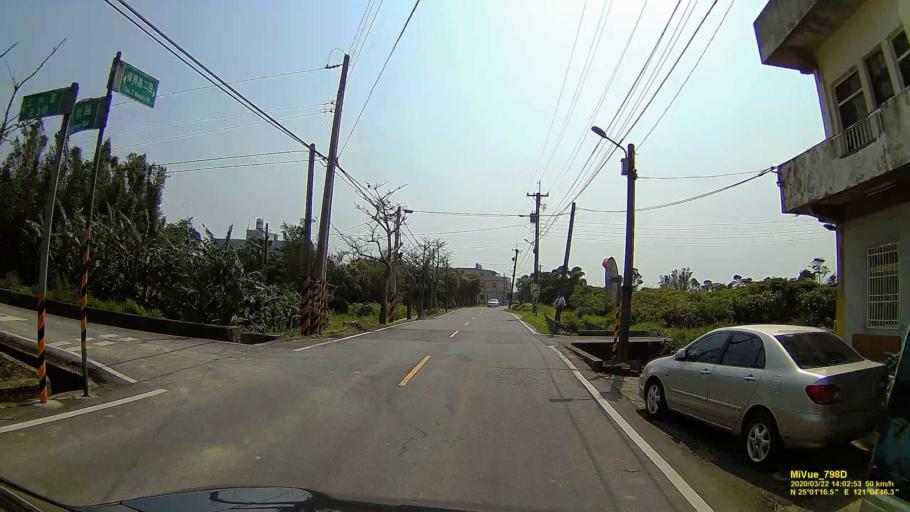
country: TW
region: Taiwan
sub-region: Hsinchu
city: Zhubei
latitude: 25.0204
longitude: 121.0785
